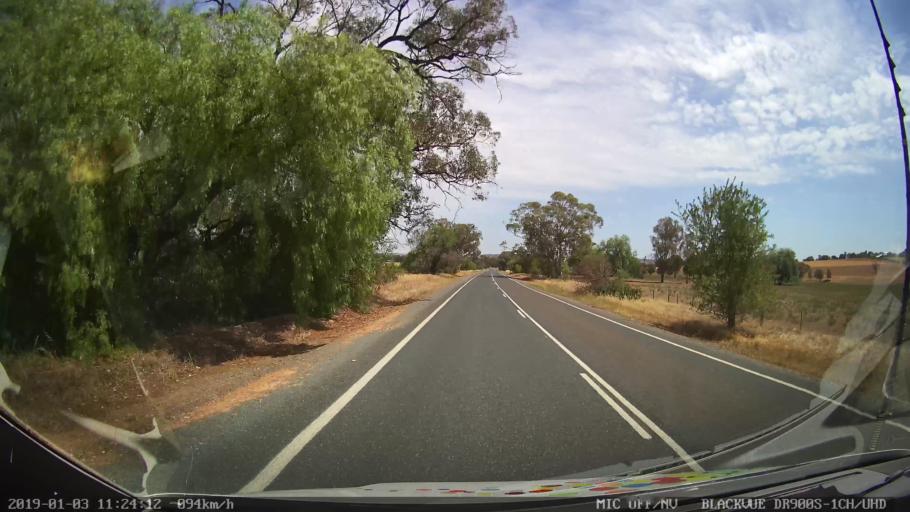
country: AU
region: New South Wales
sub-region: Weddin
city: Grenfell
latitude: -34.0544
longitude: 148.2366
